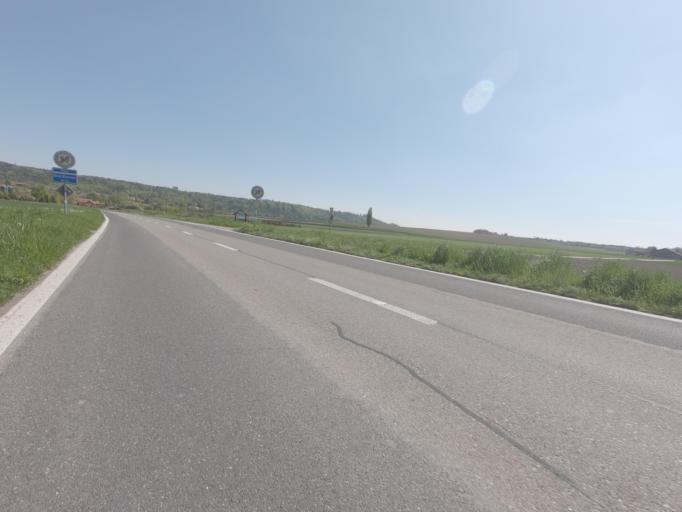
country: CH
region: Bern
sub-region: Seeland District
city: Erlach
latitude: 47.0391
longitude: 7.1006
